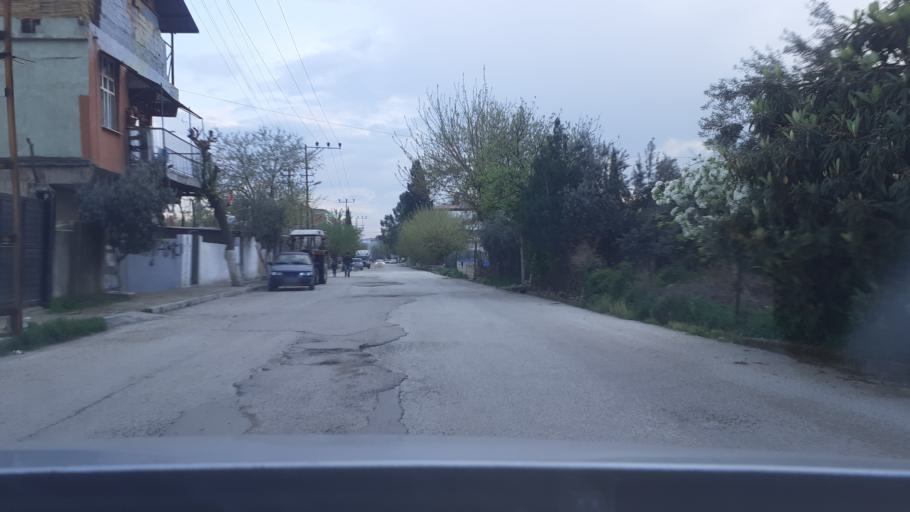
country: TR
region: Hatay
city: Kirikhan
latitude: 36.4860
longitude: 36.3504
